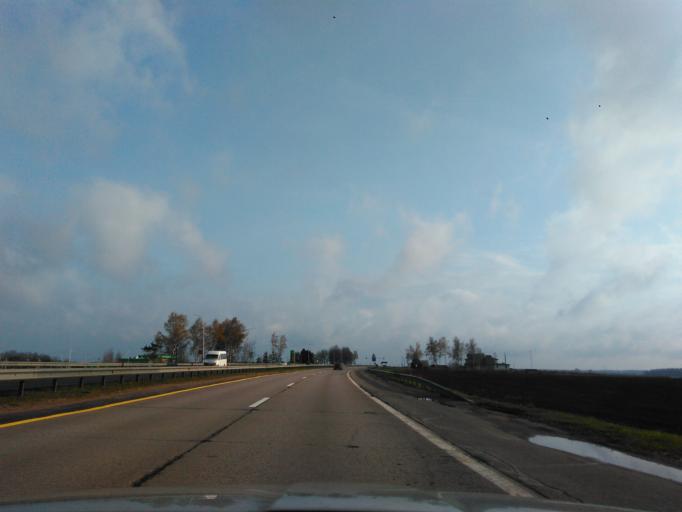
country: BY
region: Minsk
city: Lahoysk
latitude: 54.1691
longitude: 27.8187
